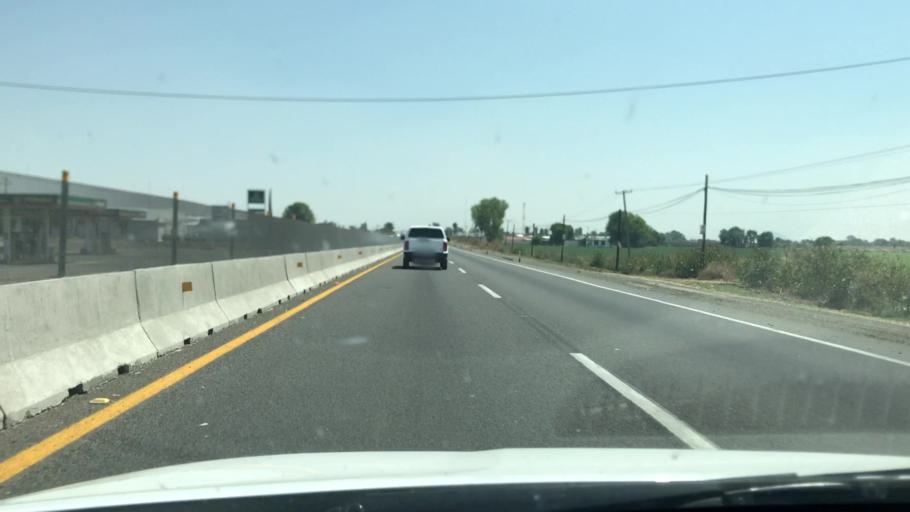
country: MX
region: Guanajuato
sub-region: Abasolo
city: San Bernardo Pena Blanca
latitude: 20.4859
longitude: -101.4915
